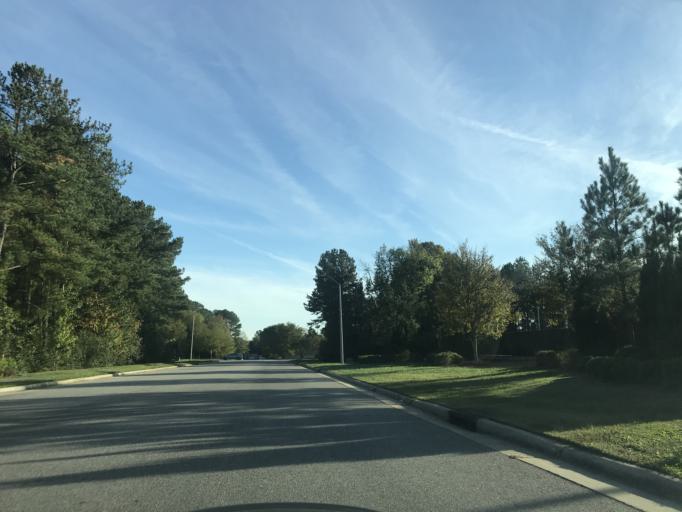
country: US
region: North Carolina
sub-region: Wake County
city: Wake Forest
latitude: 35.8924
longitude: -78.5550
